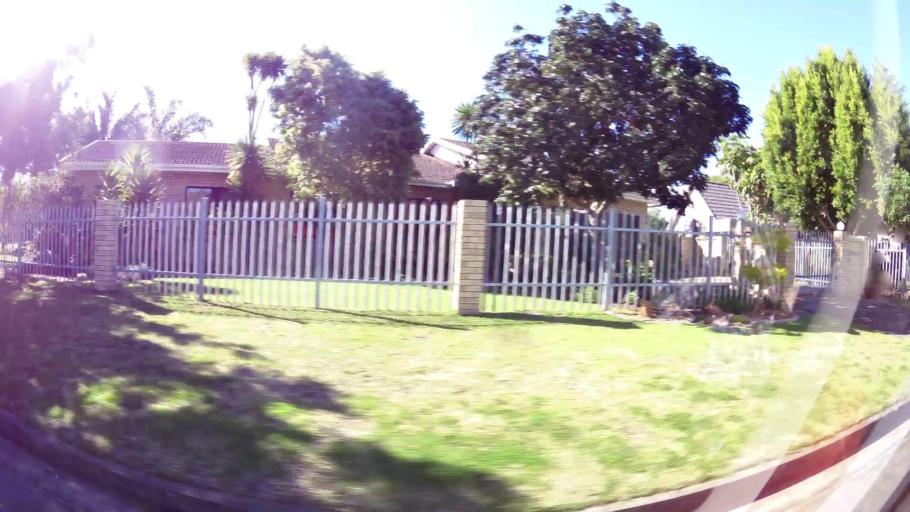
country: ZA
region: Western Cape
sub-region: Eden District Municipality
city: George
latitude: -33.9561
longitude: 22.4327
